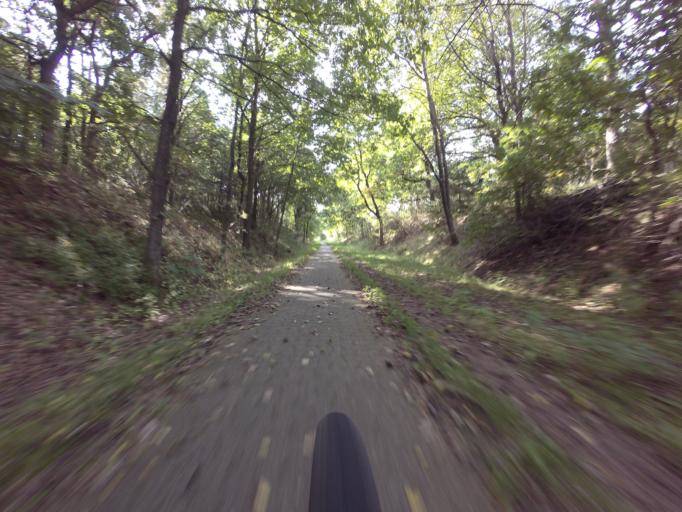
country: DK
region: Central Jutland
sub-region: Viborg Kommune
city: Viborg
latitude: 56.3895
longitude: 9.3016
